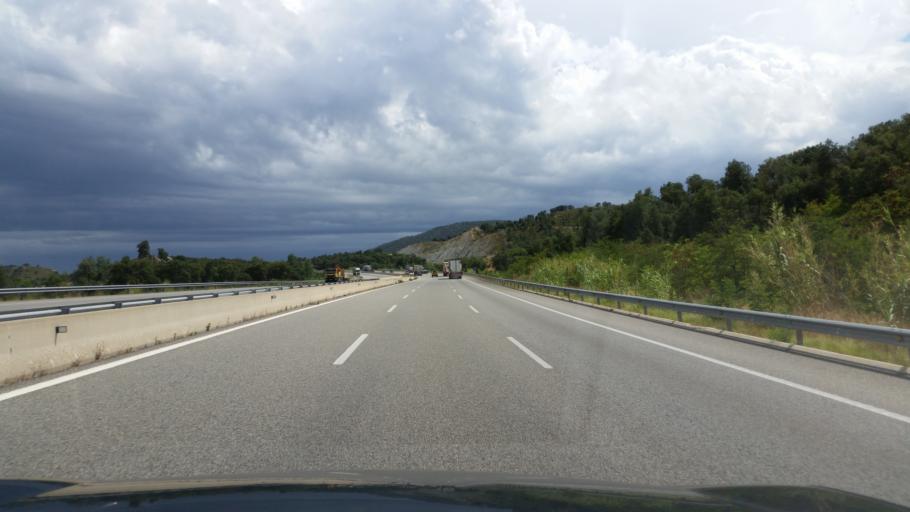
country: ES
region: Catalonia
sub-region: Provincia de Girona
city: Capmany
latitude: 42.3805
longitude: 2.8859
